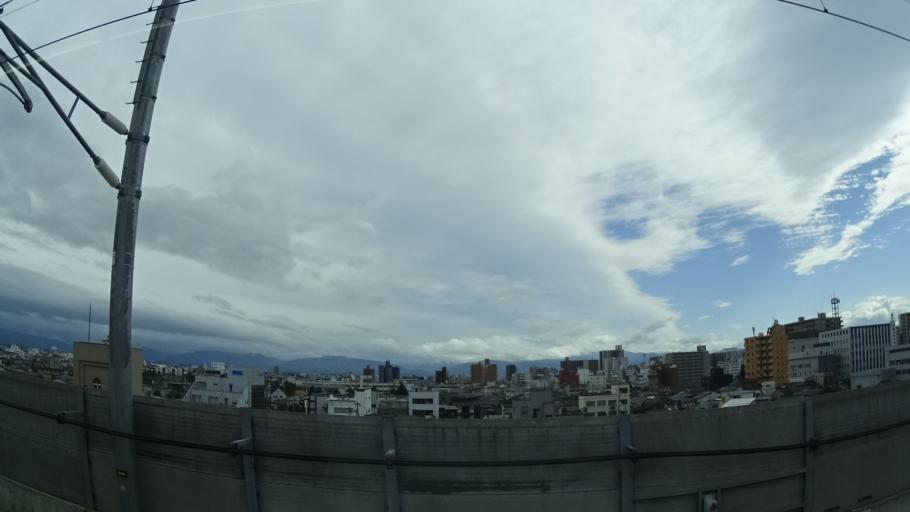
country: JP
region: Toyama
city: Toyama-shi
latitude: 36.6984
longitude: 137.2216
